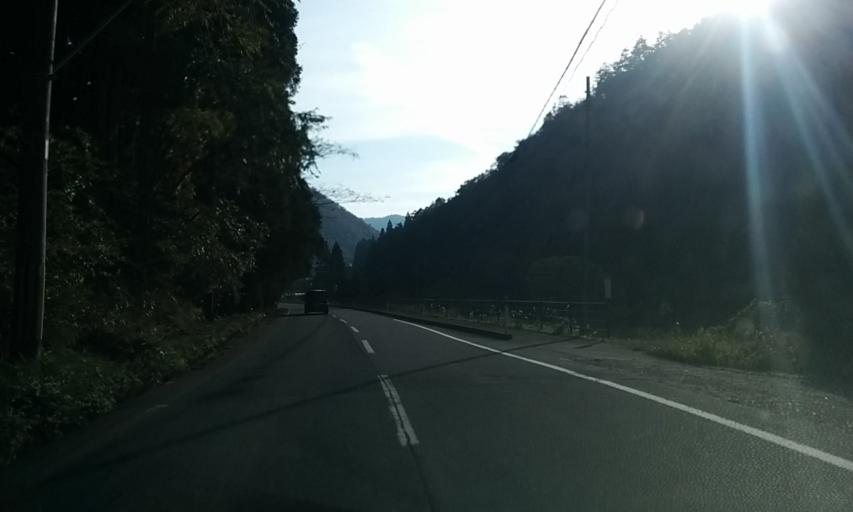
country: JP
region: Fukui
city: Obama
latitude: 35.2935
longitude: 135.6012
